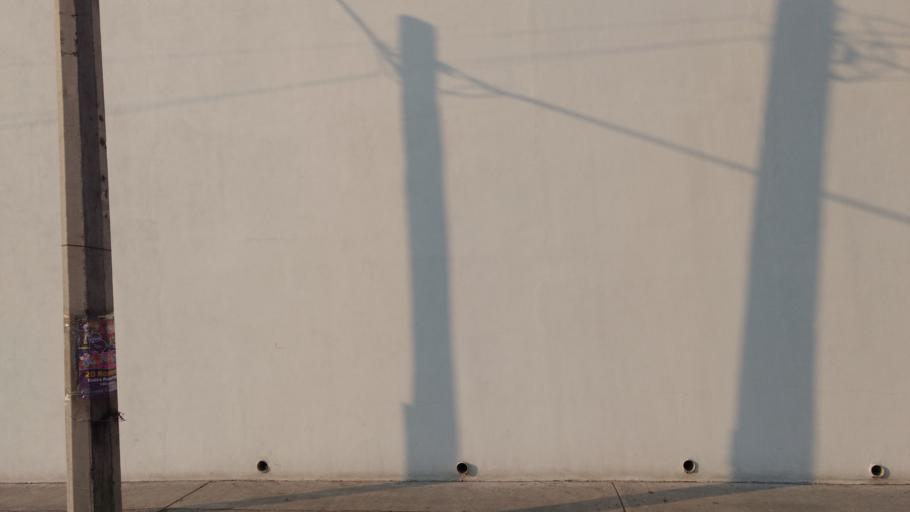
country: MX
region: Guanajuato
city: Leon
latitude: 21.1474
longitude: -101.6844
